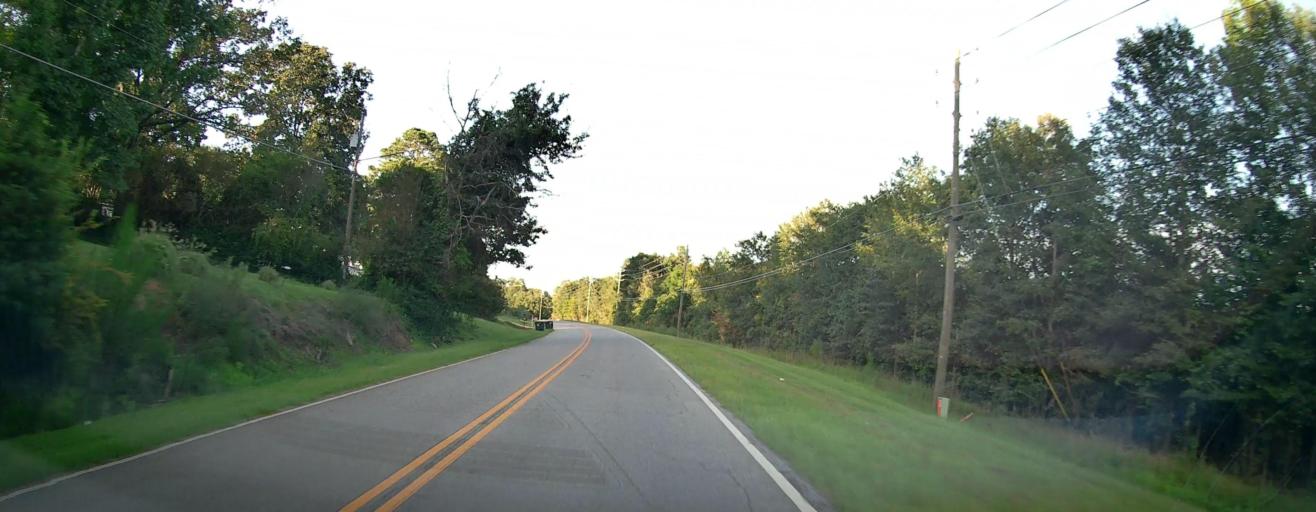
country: US
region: Georgia
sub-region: Muscogee County
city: Columbus
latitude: 32.4261
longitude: -85.0161
